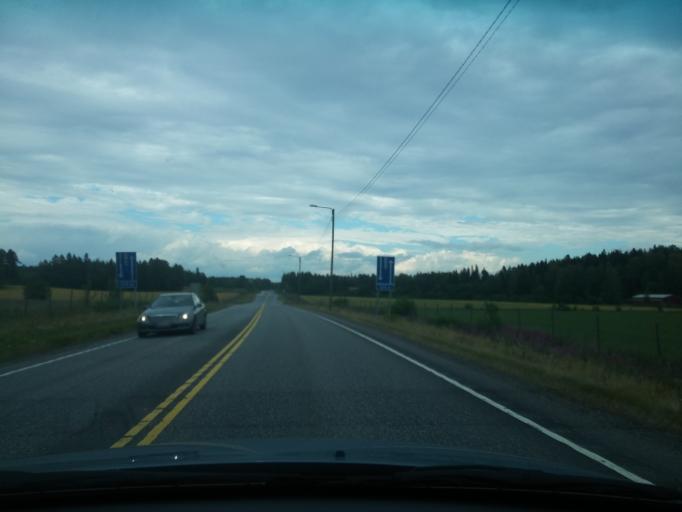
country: FI
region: Haeme
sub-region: Riihimaeki
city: Loppi
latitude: 60.7156
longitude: 24.4868
